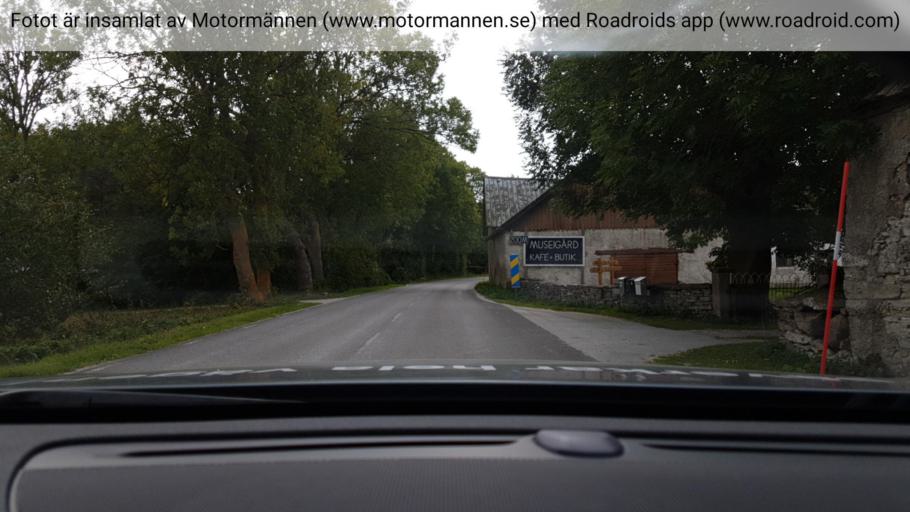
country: SE
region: Gotland
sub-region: Gotland
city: Hemse
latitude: 56.9933
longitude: 18.2486
